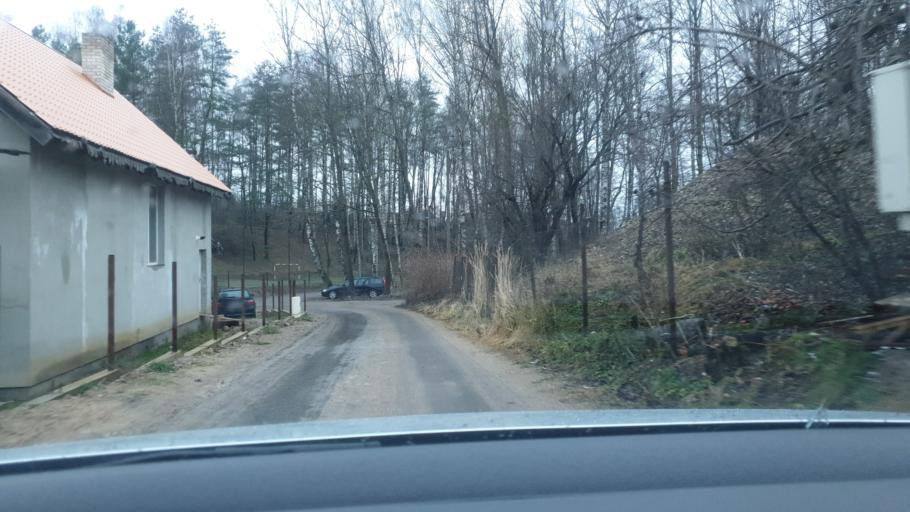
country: LT
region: Vilnius County
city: Rasos
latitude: 54.7184
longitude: 25.3811
